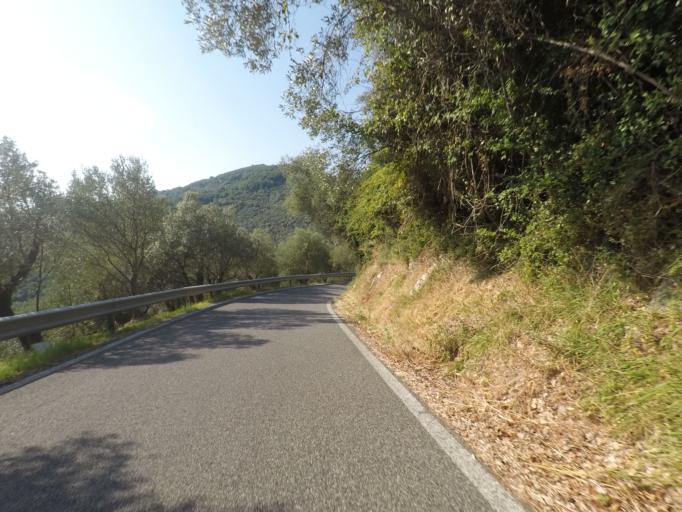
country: IT
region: Liguria
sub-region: Provincia di La Spezia
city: Casano-Dogana-Isola
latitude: 44.0895
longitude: 10.0495
